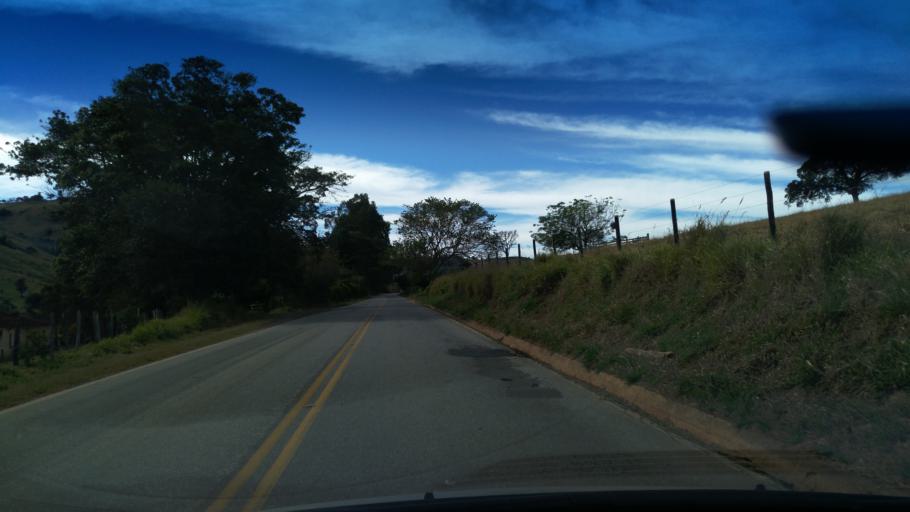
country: BR
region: Minas Gerais
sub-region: Andradas
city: Andradas
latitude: -22.0539
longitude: -46.4045
